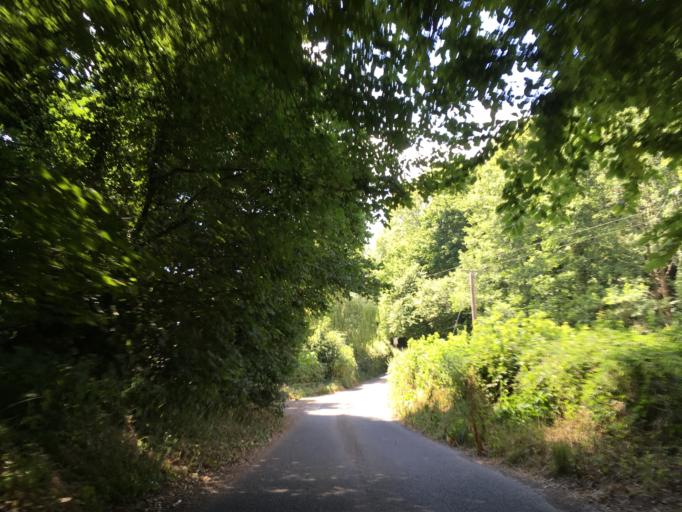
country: GB
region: England
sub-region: Gloucestershire
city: Painswick
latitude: 51.7865
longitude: -2.2070
